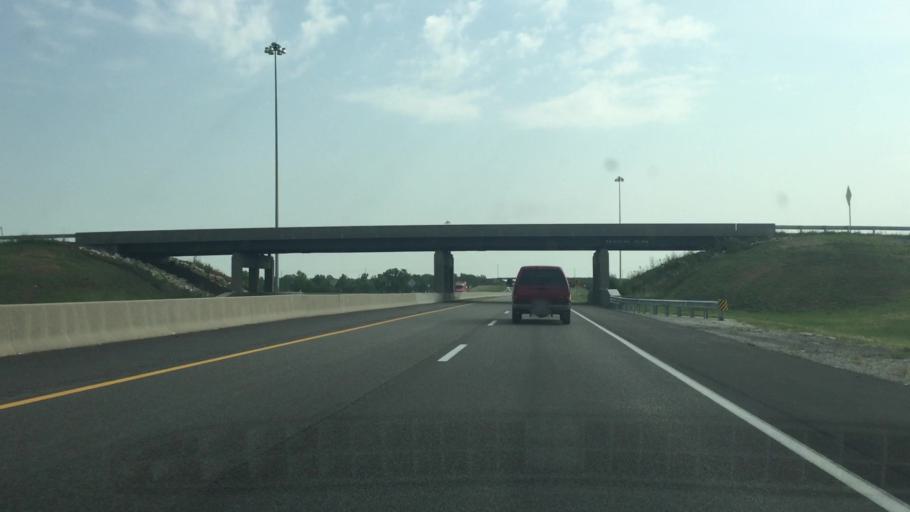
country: US
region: Kansas
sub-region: Butler County
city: El Dorado
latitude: 37.8190
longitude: -96.9032
